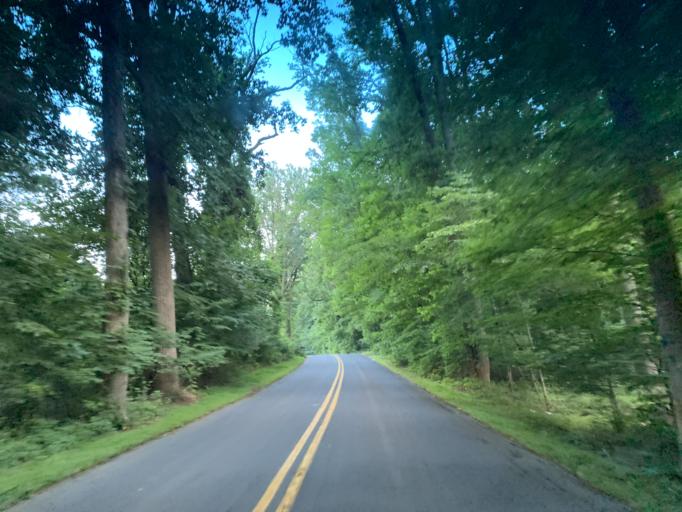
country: US
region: Maryland
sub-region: Harford County
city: Aberdeen
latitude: 39.5332
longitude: -76.1487
